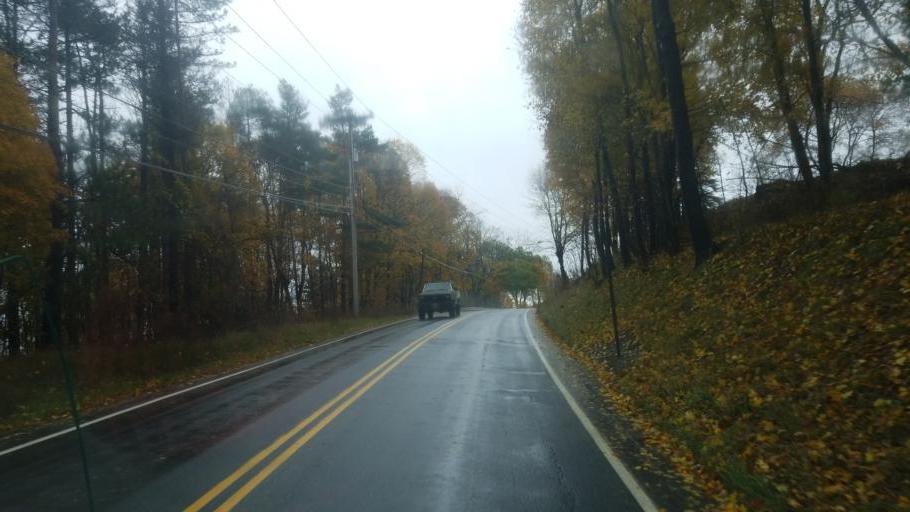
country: US
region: Pennsylvania
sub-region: Centre County
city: Milesburg
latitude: 41.0299
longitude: -77.9562
